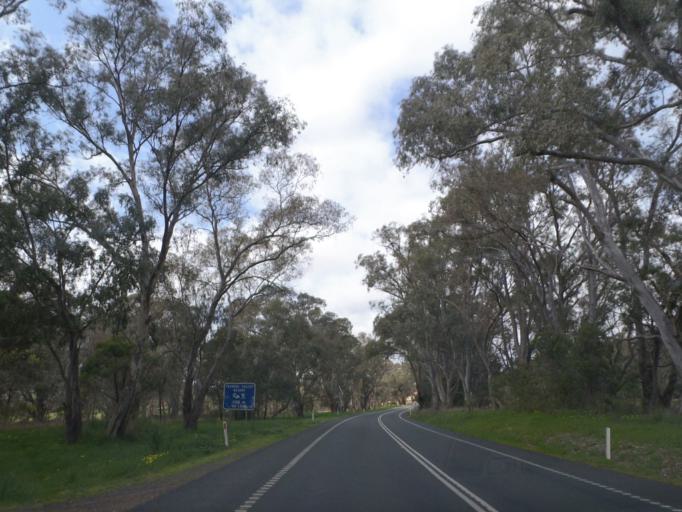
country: AU
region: Victoria
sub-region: Murrindindi
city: Kinglake West
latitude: -37.1166
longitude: 145.2129
